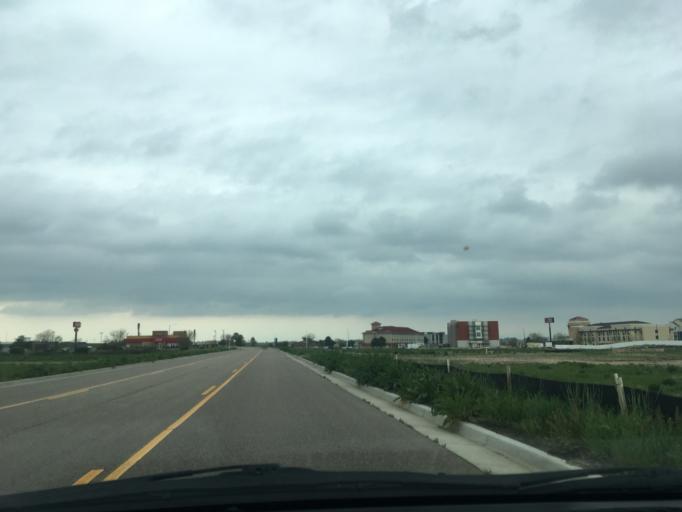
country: US
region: Colorado
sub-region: Weld County
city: Firestone
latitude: 40.1632
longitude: -104.9723
